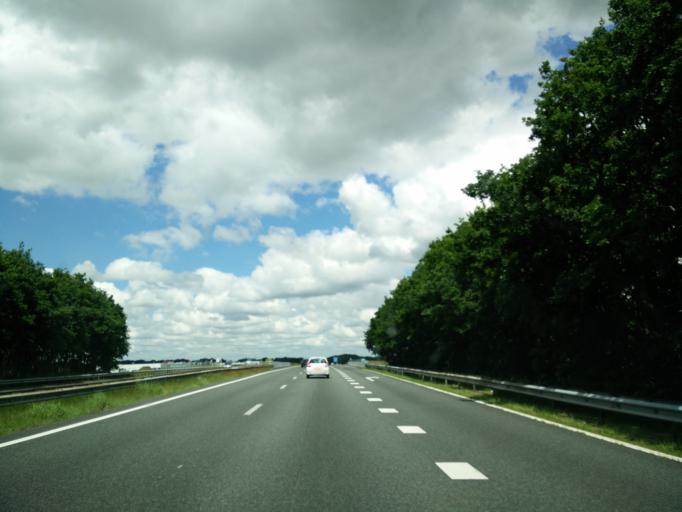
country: NL
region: Drenthe
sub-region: Gemeente Tynaarlo
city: Tynaarlo
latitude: 53.0793
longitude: 6.6037
